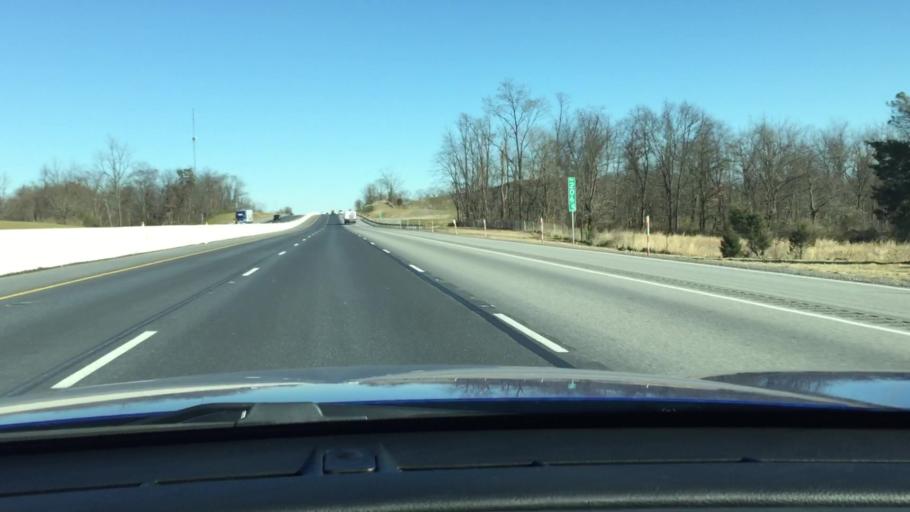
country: US
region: Pennsylvania
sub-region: Cumberland County
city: Newville
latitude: 40.1778
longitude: -77.5228
